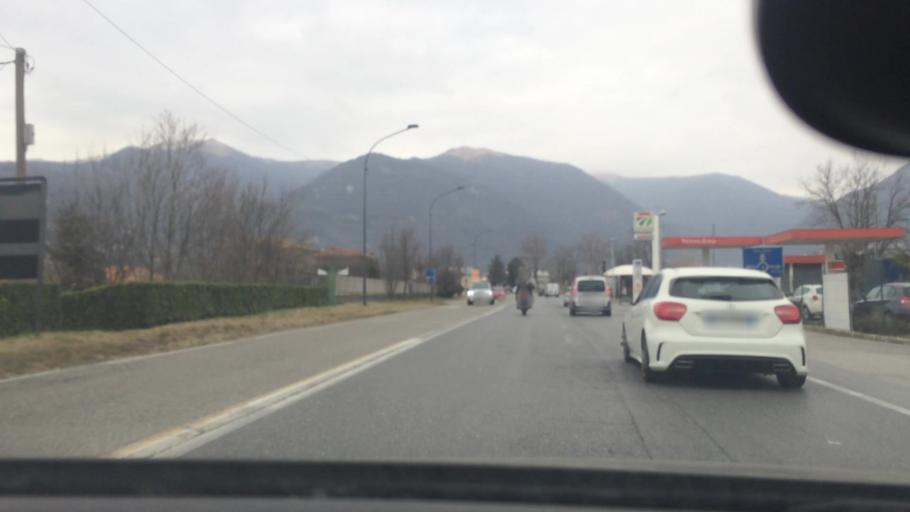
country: IT
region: Lombardy
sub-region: Provincia di Como
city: Erba
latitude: 45.8032
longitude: 9.2362
